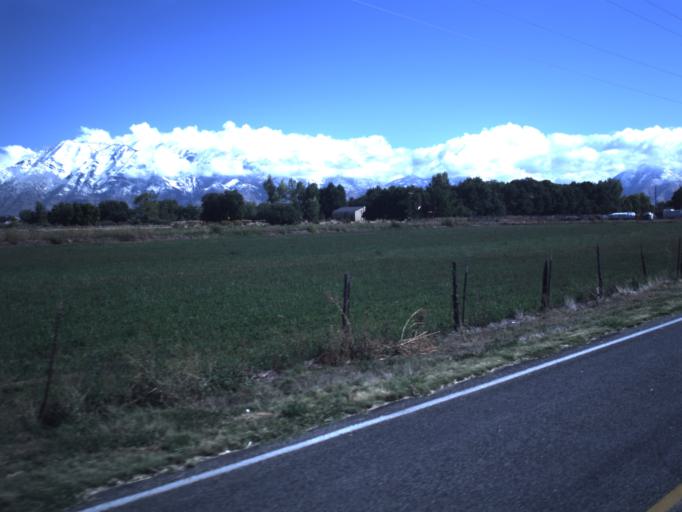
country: US
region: Utah
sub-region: Utah County
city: Benjamin
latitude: 40.0983
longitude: -111.6956
